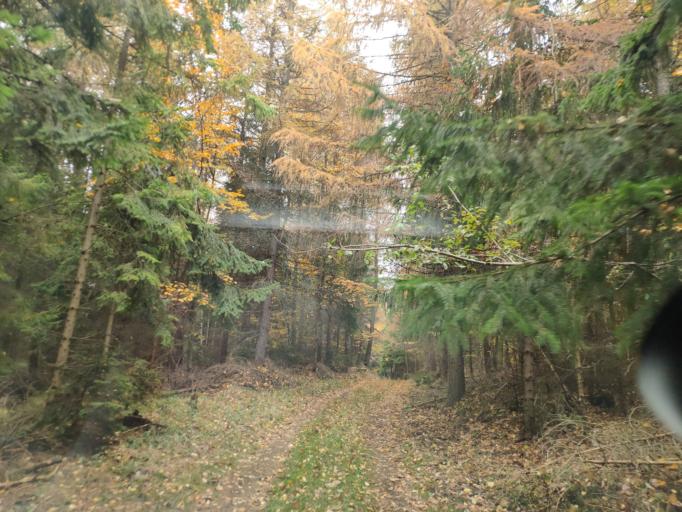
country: SK
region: Kosicky
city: Medzev
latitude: 48.7451
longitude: 20.9884
